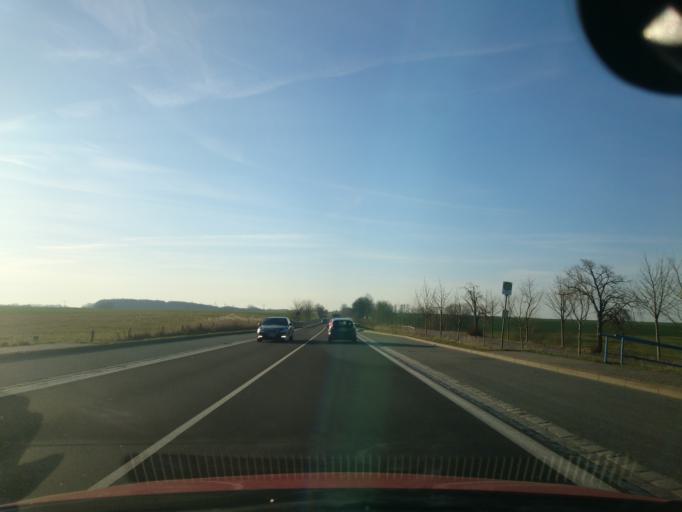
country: DE
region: Mecklenburg-Vorpommern
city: Brandshagen
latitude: 54.2309
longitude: 13.2007
